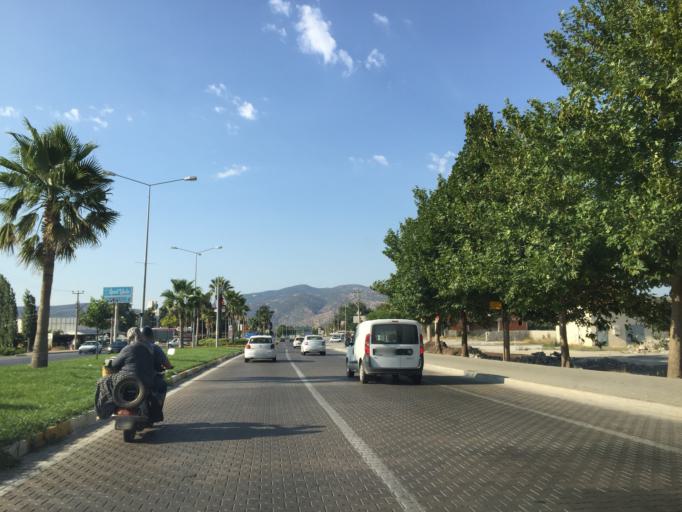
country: TR
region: Izmir
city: Selcuk
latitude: 37.9596
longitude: 27.3723
